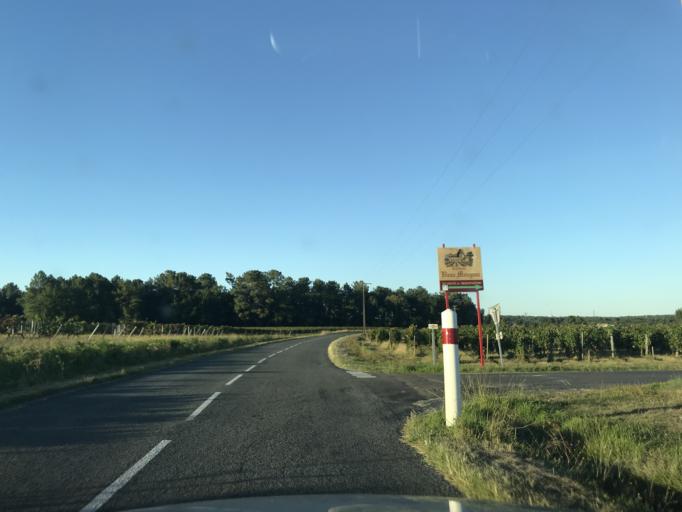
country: FR
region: Aquitaine
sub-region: Departement de la Gironde
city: Lussac
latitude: 44.9727
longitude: -0.0690
